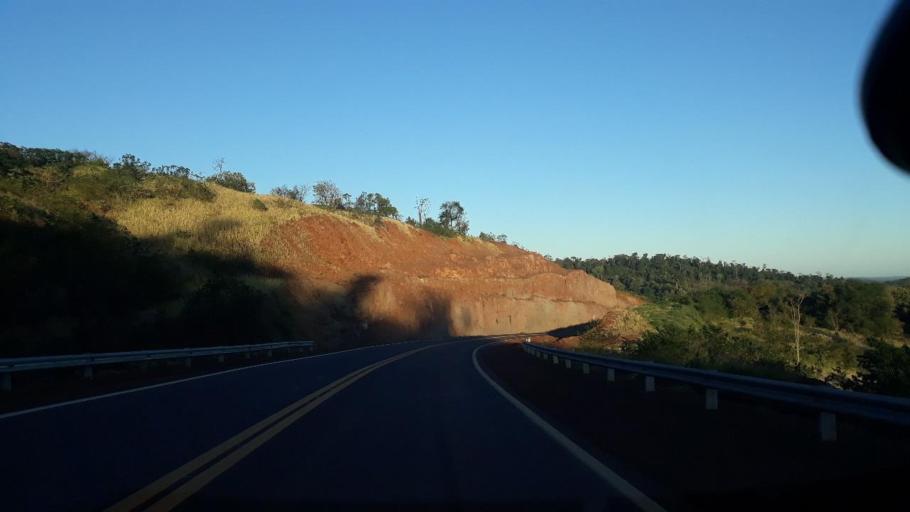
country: AR
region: Misiones
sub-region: Departamento de San Pedro
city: San Pedro
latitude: -26.5394
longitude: -53.9431
